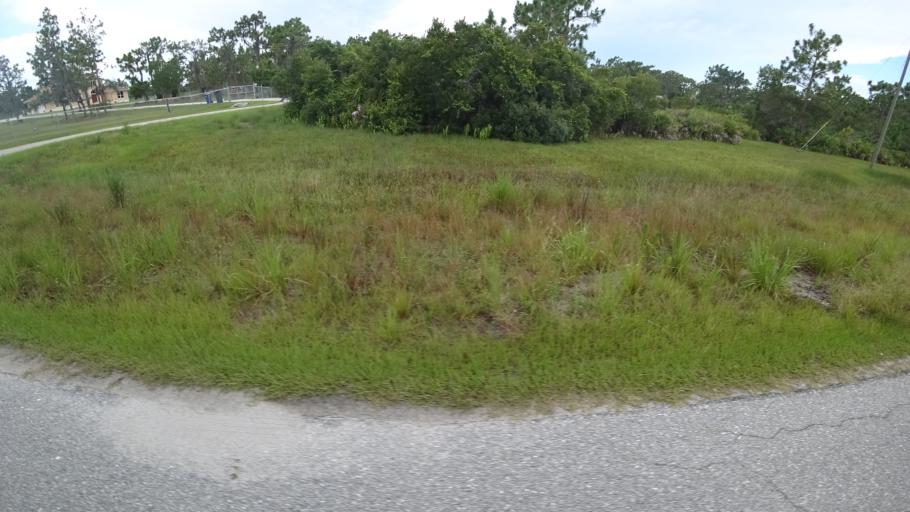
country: US
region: Florida
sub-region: Sarasota County
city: The Meadows
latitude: 27.4126
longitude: -82.2838
